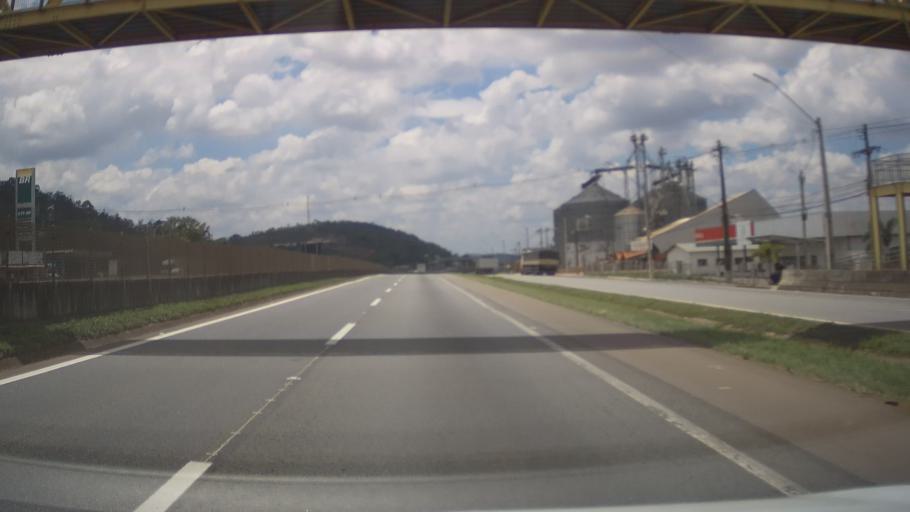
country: BR
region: Minas Gerais
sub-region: Tres Coracoes
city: Tres Coracoes
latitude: -21.6688
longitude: -45.3254
